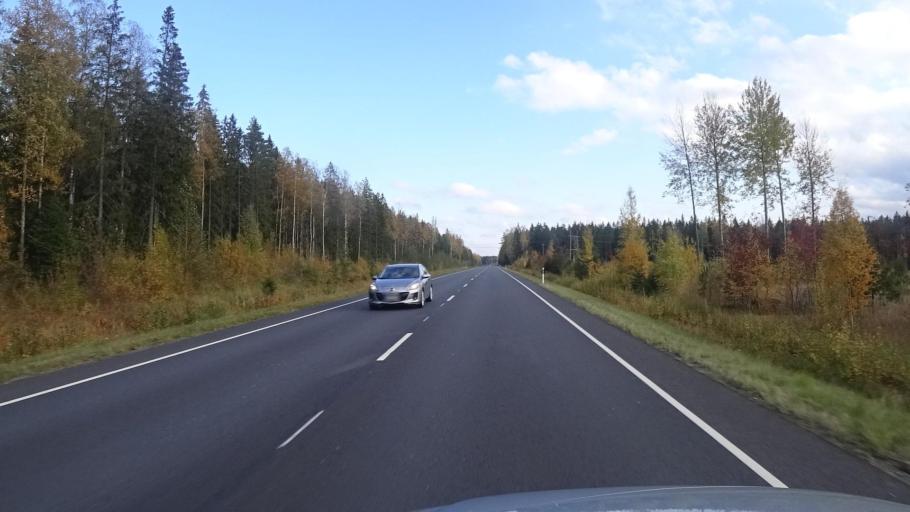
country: FI
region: Satakunta
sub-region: Rauma
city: Eura
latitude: 61.1144
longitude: 22.1973
